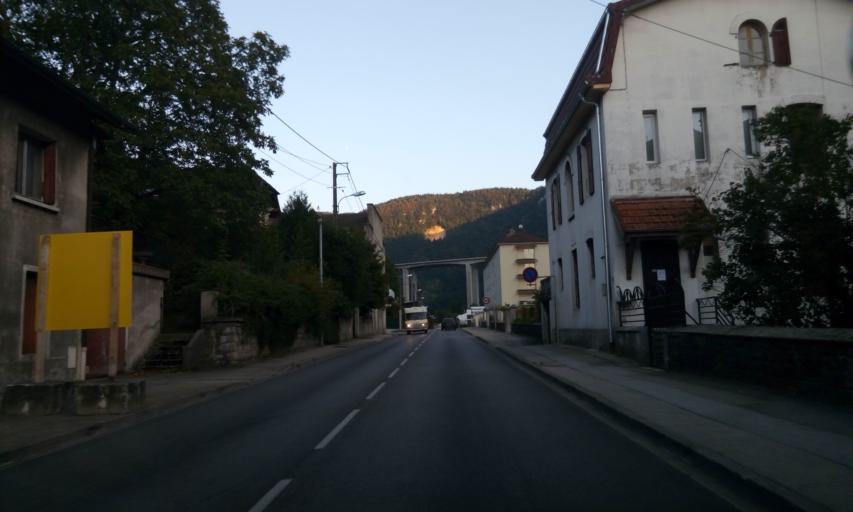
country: FR
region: Rhone-Alpes
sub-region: Departement de l'Ain
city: Nantua
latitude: 46.1484
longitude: 5.6090
